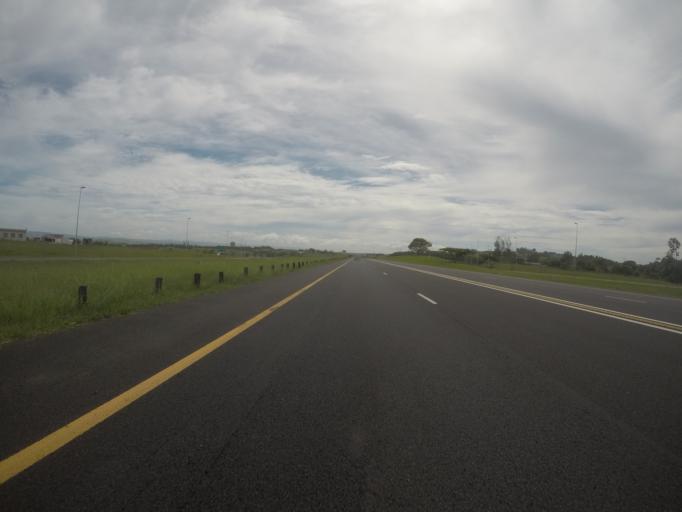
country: ZA
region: KwaZulu-Natal
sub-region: iLembe District Municipality
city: Mandeni
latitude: -29.0806
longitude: 31.6125
